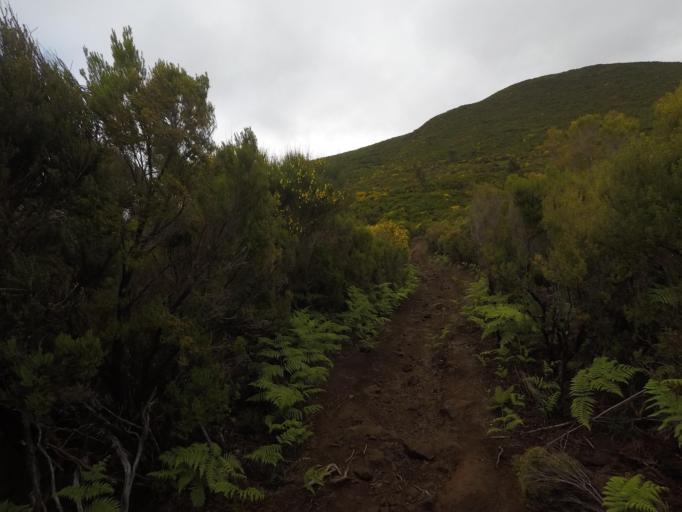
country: PT
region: Madeira
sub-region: Calheta
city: Arco da Calheta
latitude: 32.7764
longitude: -17.1329
